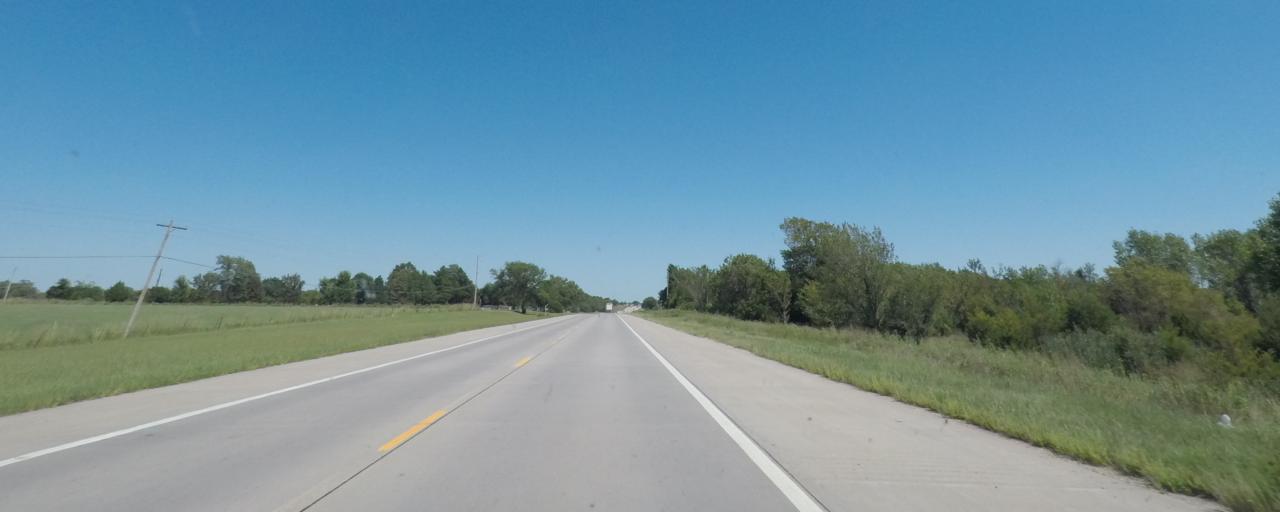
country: US
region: Kansas
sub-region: Lyon County
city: Emporia
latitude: 38.4120
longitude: -96.2756
